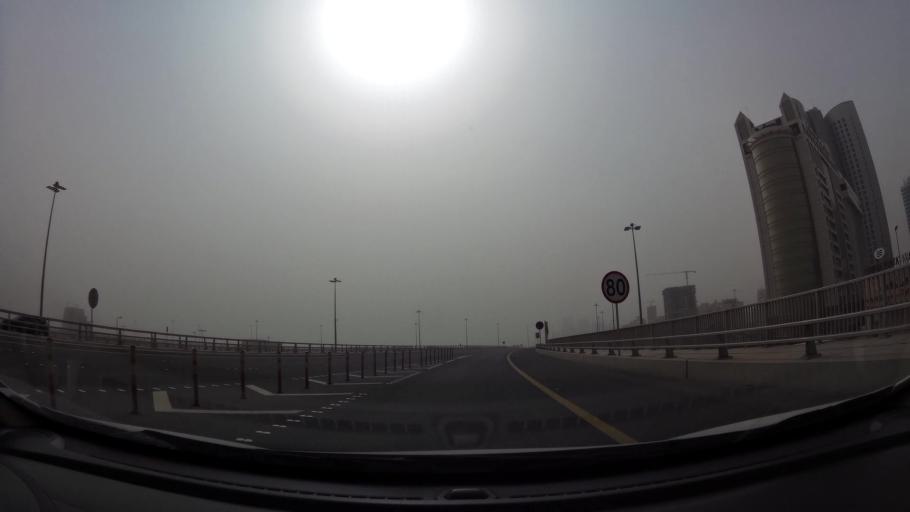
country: BH
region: Muharraq
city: Al Muharraq
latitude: 26.2442
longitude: 50.5922
